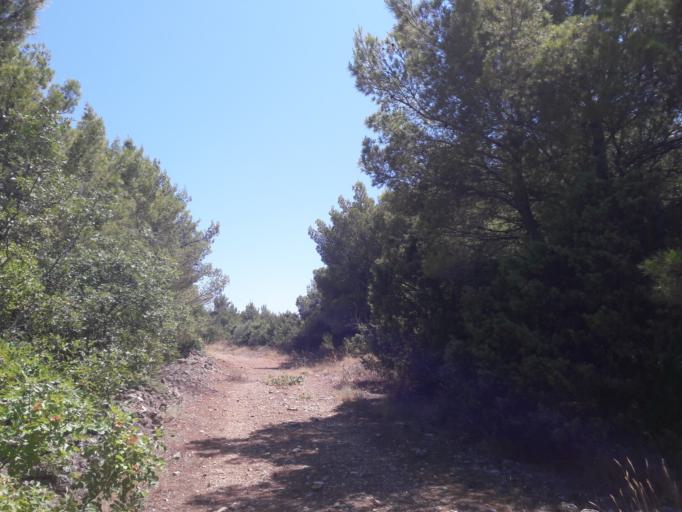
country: HR
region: Sibensko-Kniniska
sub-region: Grad Sibenik
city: Sibenik
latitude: 43.6924
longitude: 15.8545
